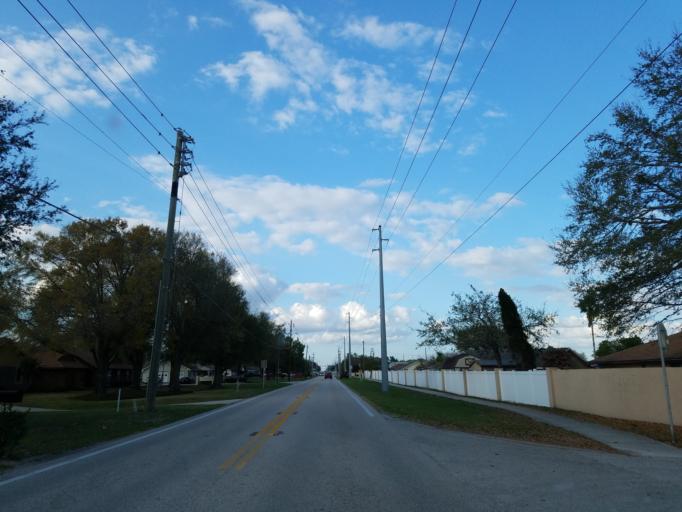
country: US
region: Florida
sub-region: Polk County
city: Lakeland Highlands
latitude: 27.9478
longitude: -81.9236
